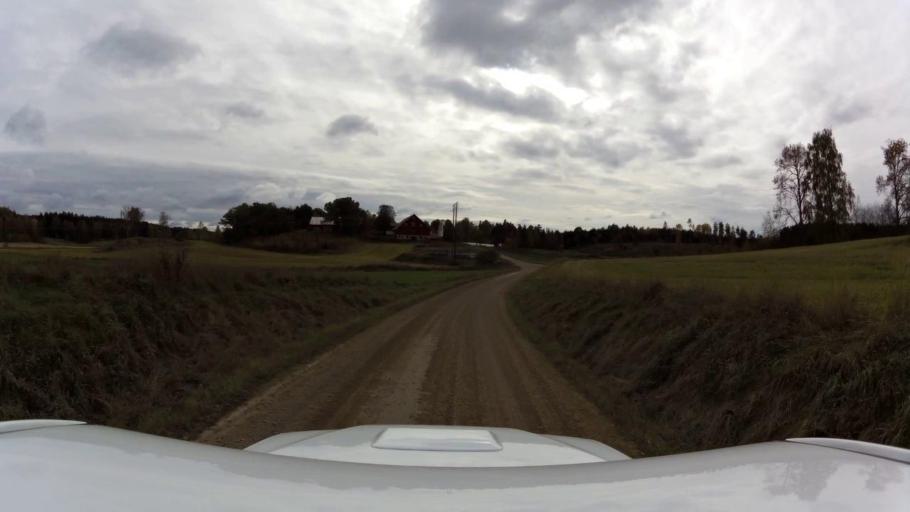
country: SE
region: OEstergoetland
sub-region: Linkopings Kommun
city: Ekangen
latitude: 58.5605
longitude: 15.6610
